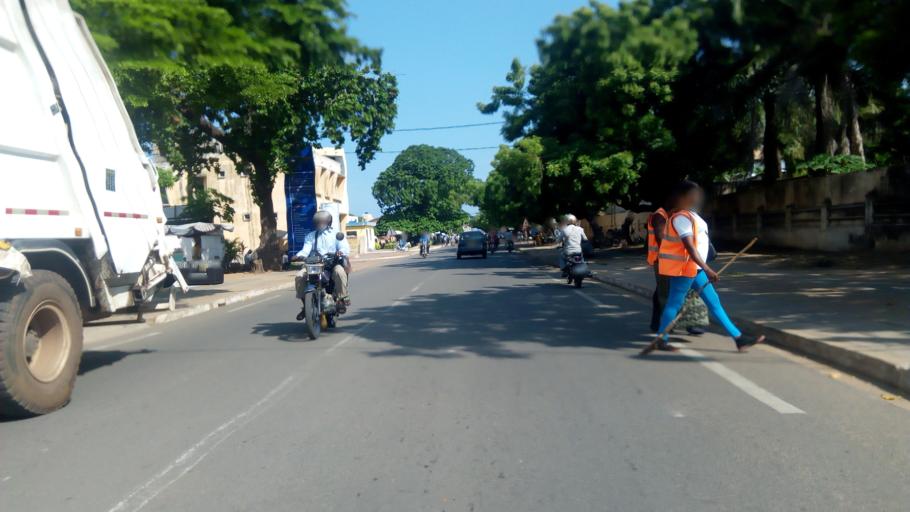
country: TG
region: Maritime
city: Lome
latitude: 6.1342
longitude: 1.2228
